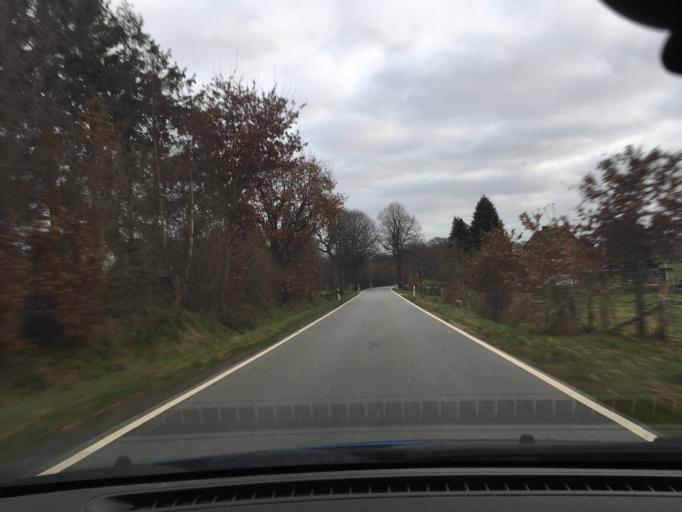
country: DE
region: Schleswig-Holstein
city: Agethorst
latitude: 54.0127
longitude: 9.4325
